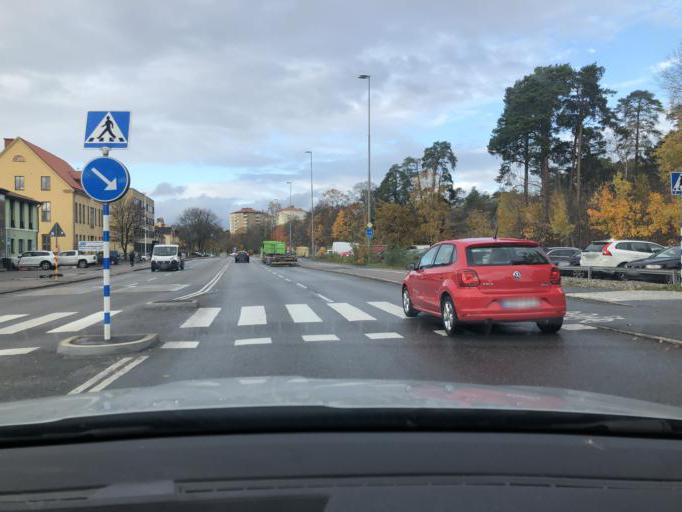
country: SE
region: Stockholm
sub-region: Stockholms Kommun
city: Arsta
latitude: 59.2935
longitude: 18.0728
